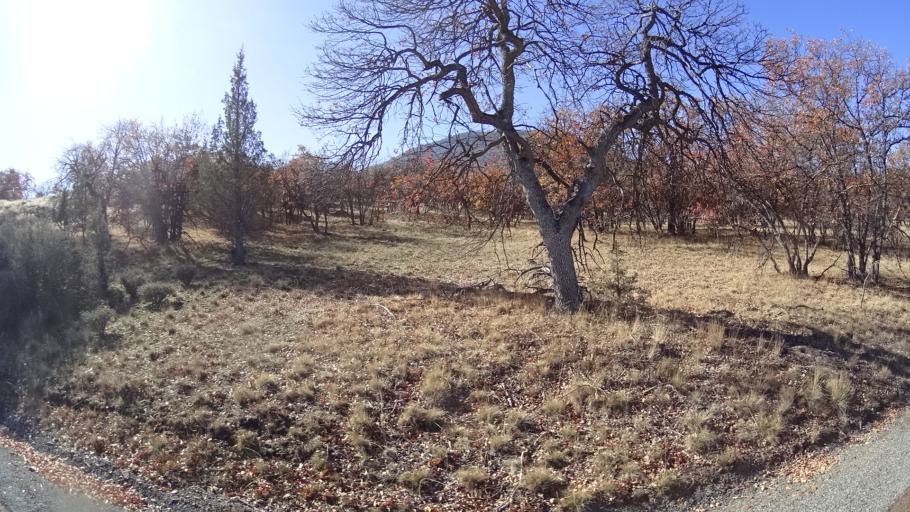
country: US
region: California
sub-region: Siskiyou County
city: Montague
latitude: 41.8805
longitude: -122.4843
